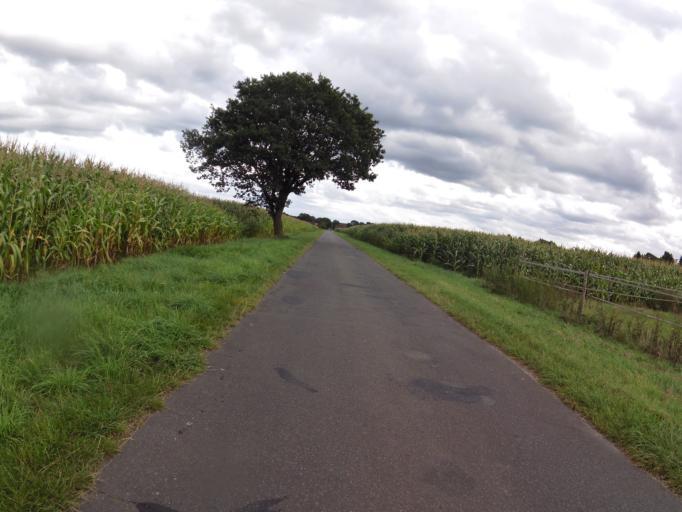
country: DE
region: Lower Saxony
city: Kohlen
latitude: 53.5120
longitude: 8.8524
